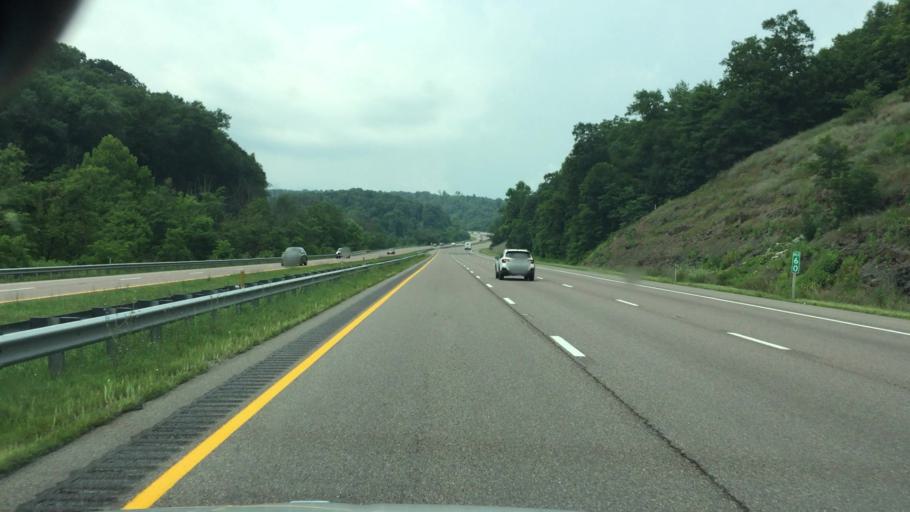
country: US
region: Maryland
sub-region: Allegany County
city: Cumberland
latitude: 39.6864
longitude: -78.4986
